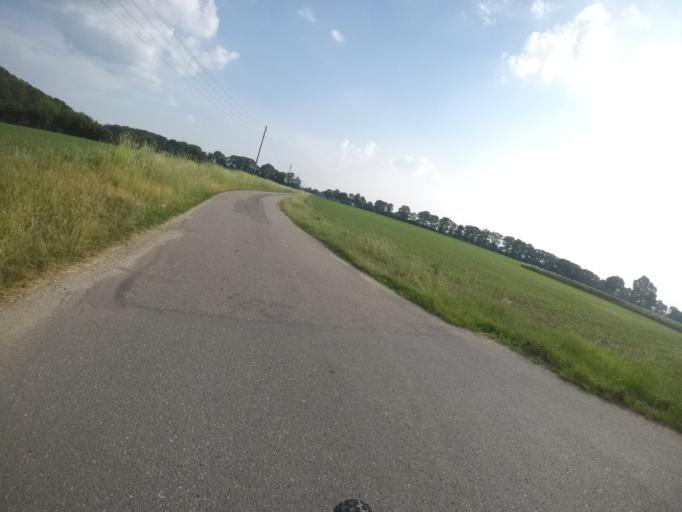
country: DE
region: North Rhine-Westphalia
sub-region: Regierungsbezirk Munster
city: Isselburg
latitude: 51.8433
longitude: 6.4879
